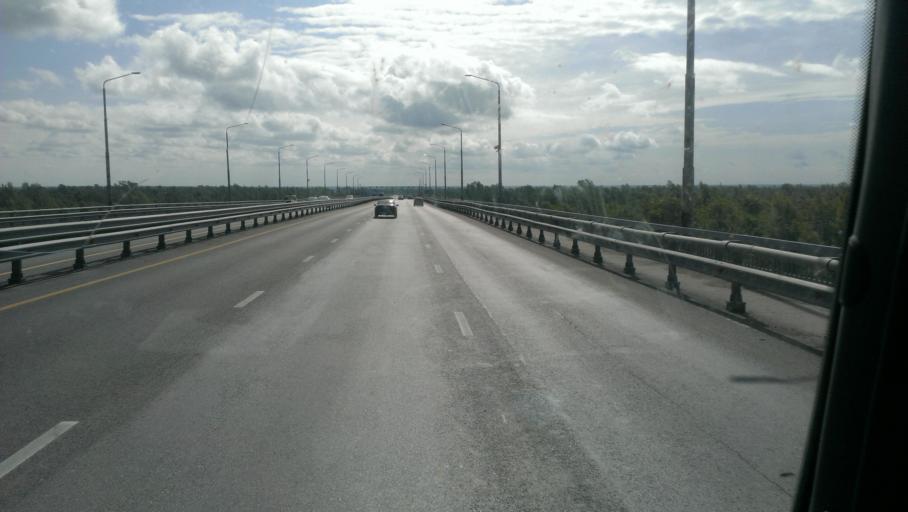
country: RU
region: Altai Krai
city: Zaton
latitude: 53.3226
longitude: 83.8059
